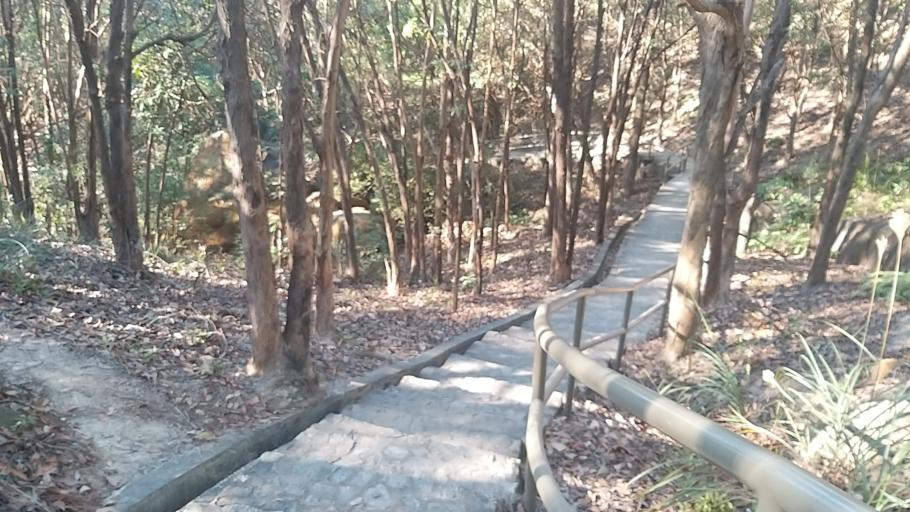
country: HK
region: Tuen Mun
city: Tuen Mun
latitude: 22.3999
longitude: 113.9847
